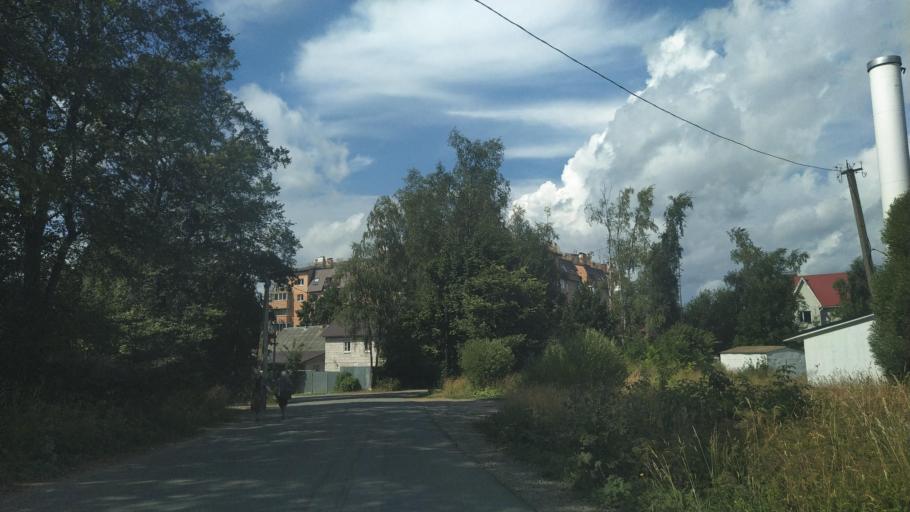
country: RU
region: Leningrad
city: Toksovo
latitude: 60.1659
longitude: 30.5404
